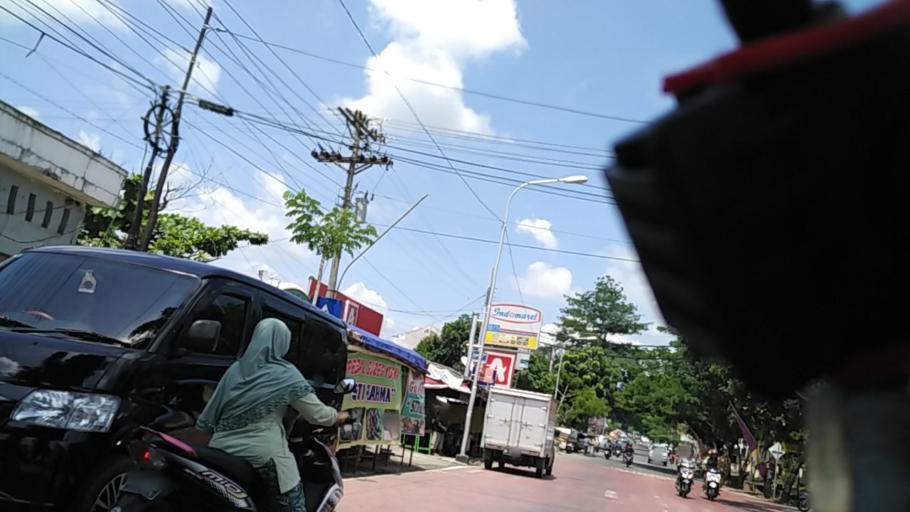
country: ID
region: Central Java
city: Semarang
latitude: -7.0516
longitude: 110.4262
